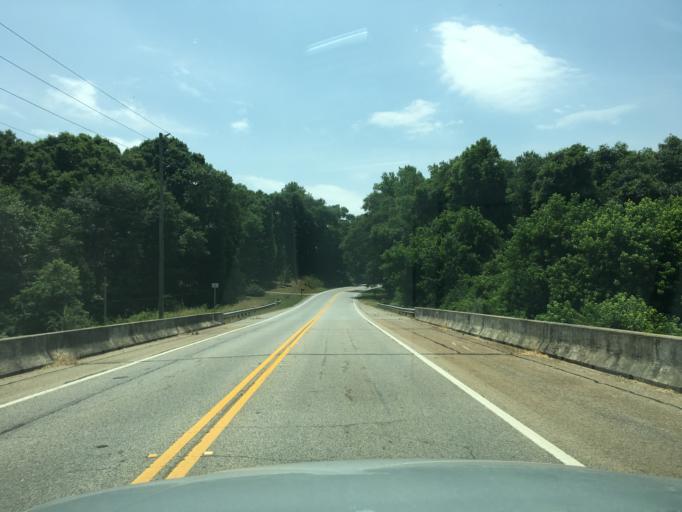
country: US
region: Georgia
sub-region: Hart County
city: Royston
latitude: 34.2473
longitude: -83.1732
